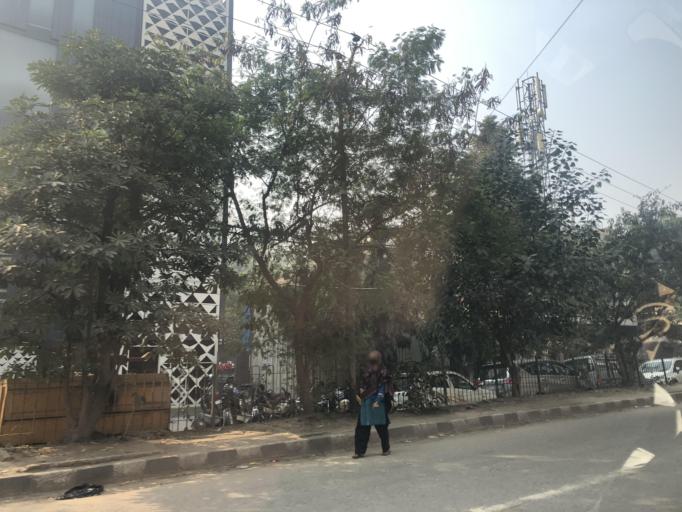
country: IN
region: NCT
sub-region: West Delhi
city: Nangloi Jat
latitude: 28.6789
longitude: 77.0997
